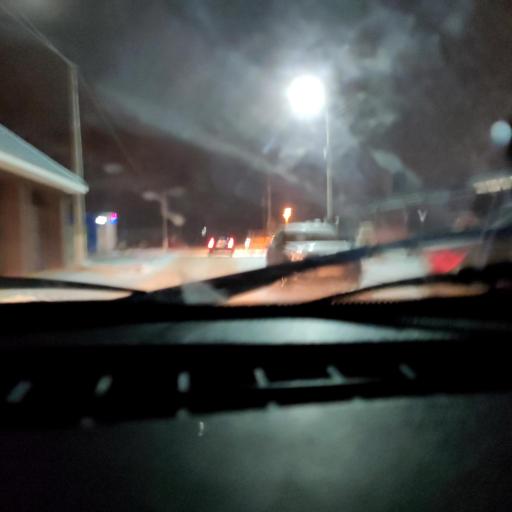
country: RU
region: Bashkortostan
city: Kabakovo
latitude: 54.6328
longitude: 56.1139
